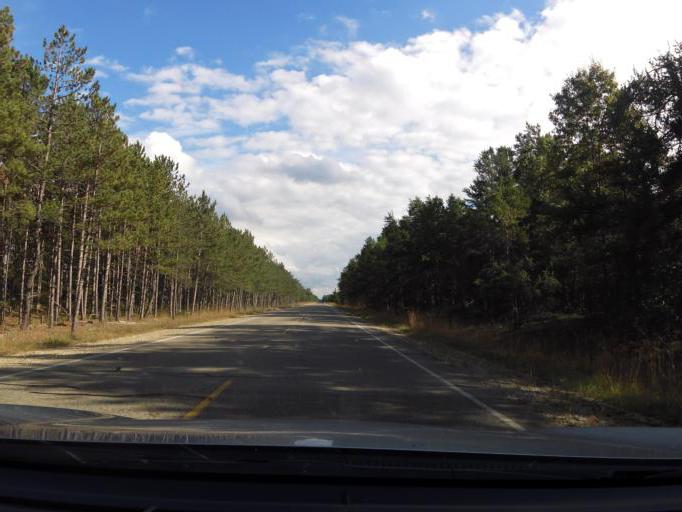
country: US
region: Michigan
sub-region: Roscommon County
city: Roscommon
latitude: 44.4803
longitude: -84.5617
